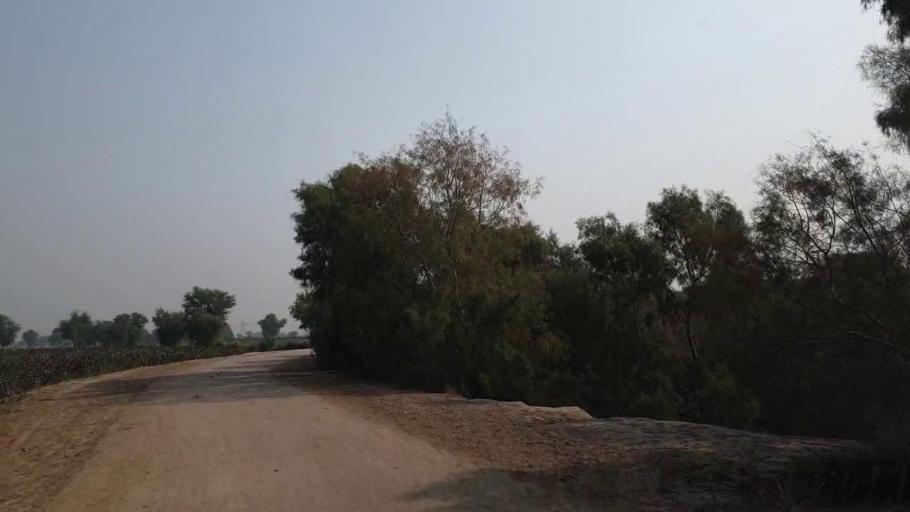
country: PK
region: Sindh
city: Bhan
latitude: 26.5176
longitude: 67.7379
